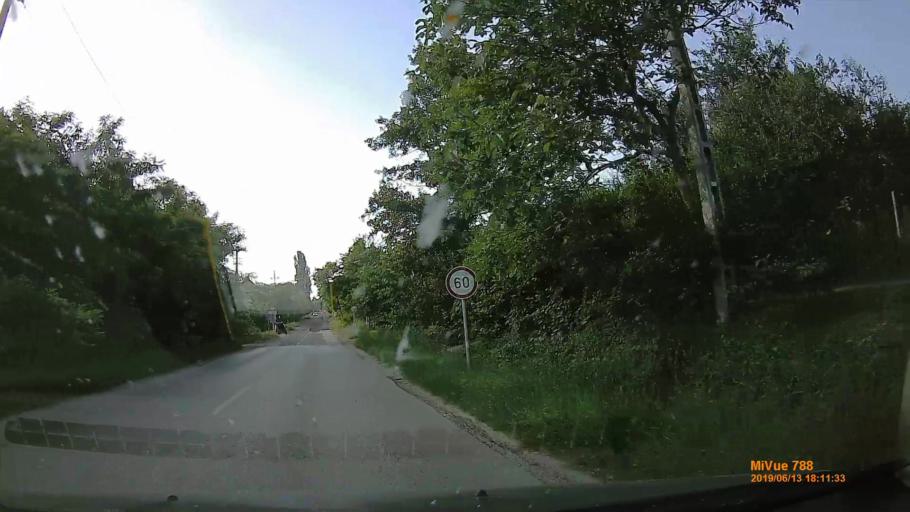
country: HU
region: Pest
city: Ecser
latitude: 47.4562
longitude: 19.3015
